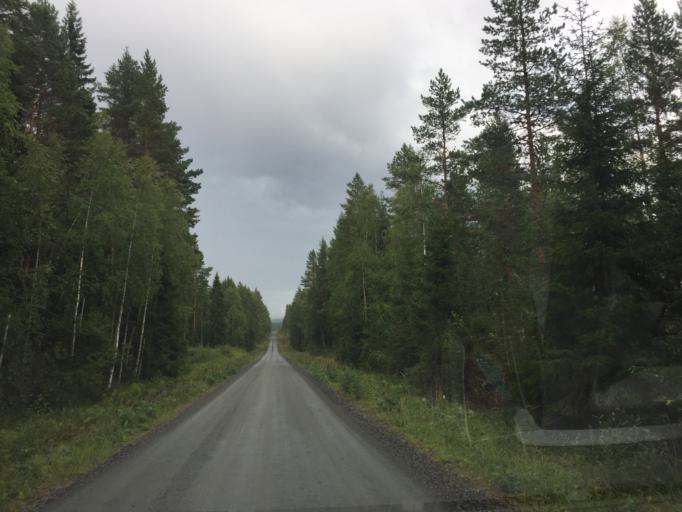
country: SE
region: Vaermland
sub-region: Filipstads Kommun
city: Lesjofors
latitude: 59.9106
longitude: 14.1058
